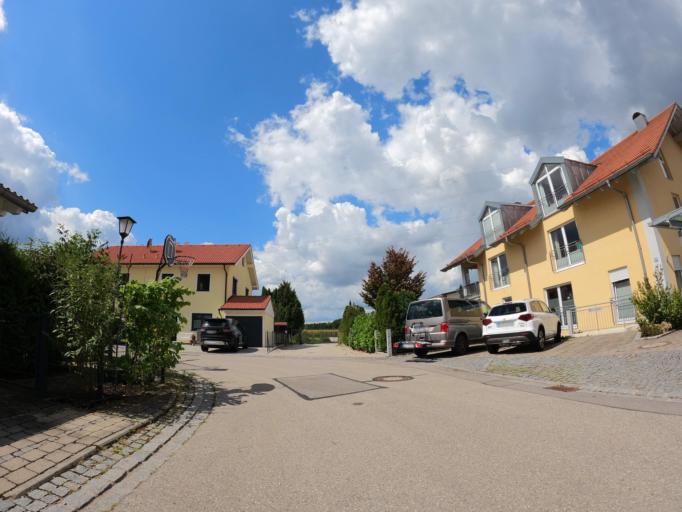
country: DE
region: Bavaria
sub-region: Upper Bavaria
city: Brunnthal
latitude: 48.0079
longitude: 11.6779
